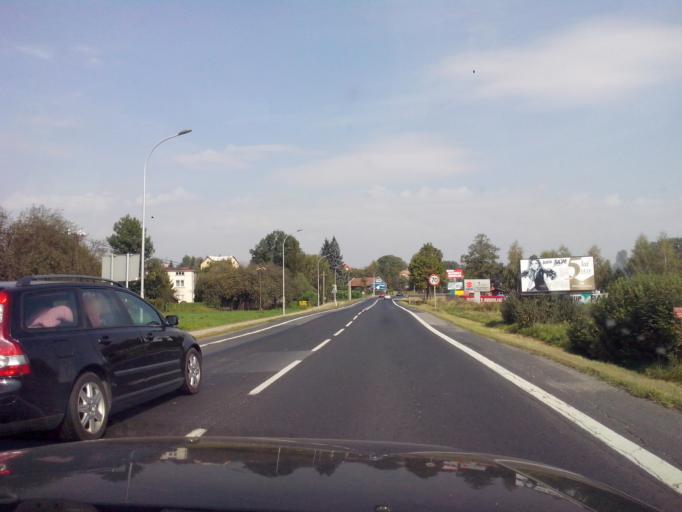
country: PL
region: Subcarpathian Voivodeship
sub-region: Powiat rzeszowski
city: Lutoryz
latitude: 49.9581
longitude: 21.9168
